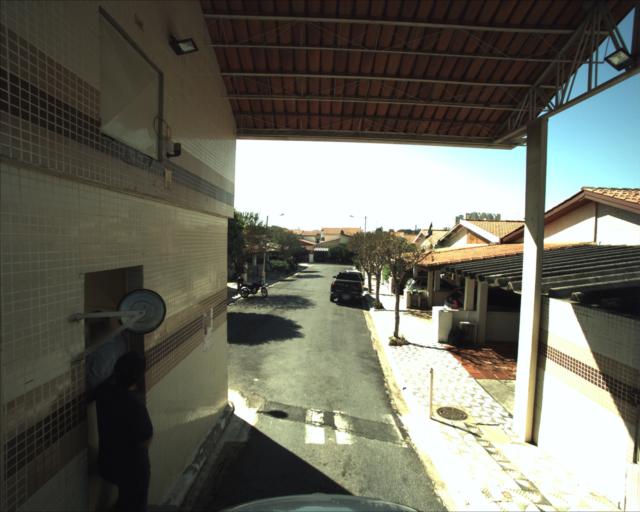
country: BR
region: Sao Paulo
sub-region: Sorocaba
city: Sorocaba
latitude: -23.4919
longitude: -47.4376
